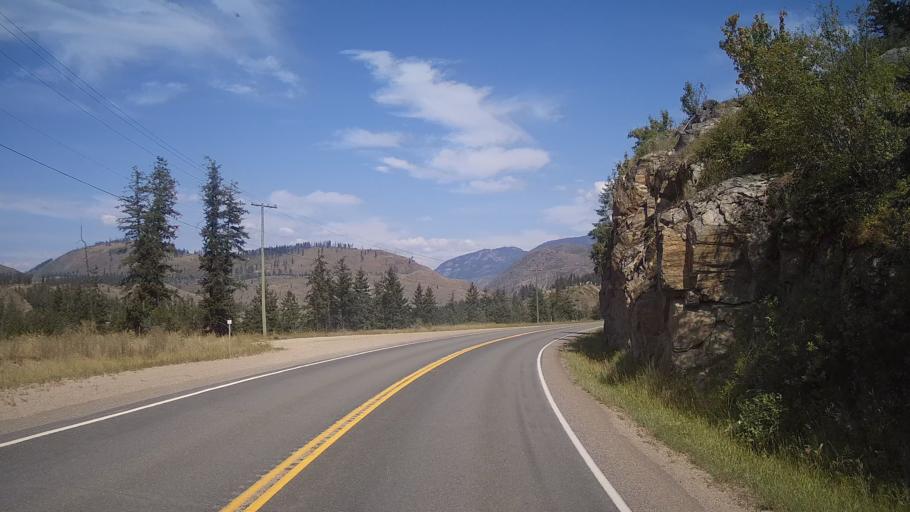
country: CA
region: British Columbia
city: Kamloops
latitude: 51.0857
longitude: -120.1817
